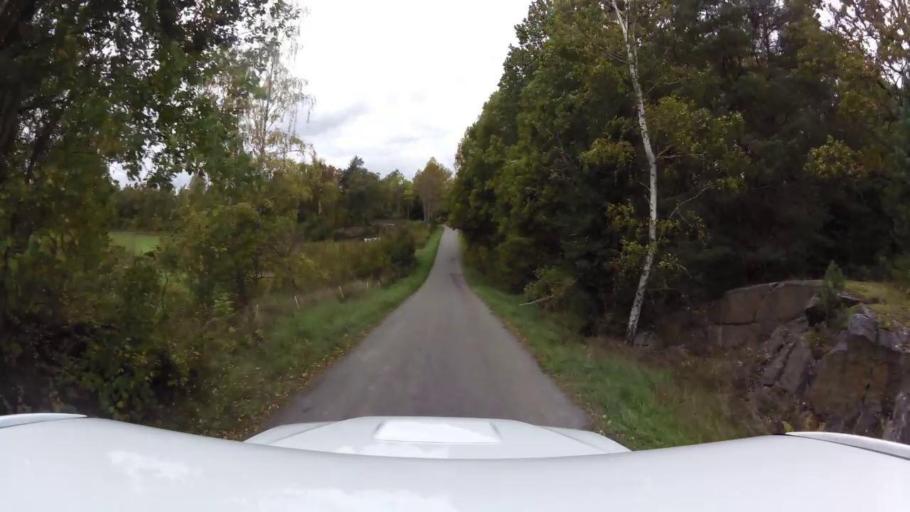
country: SE
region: OEstergoetland
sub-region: Kinda Kommun
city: Rimforsa
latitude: 58.1940
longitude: 15.6132
